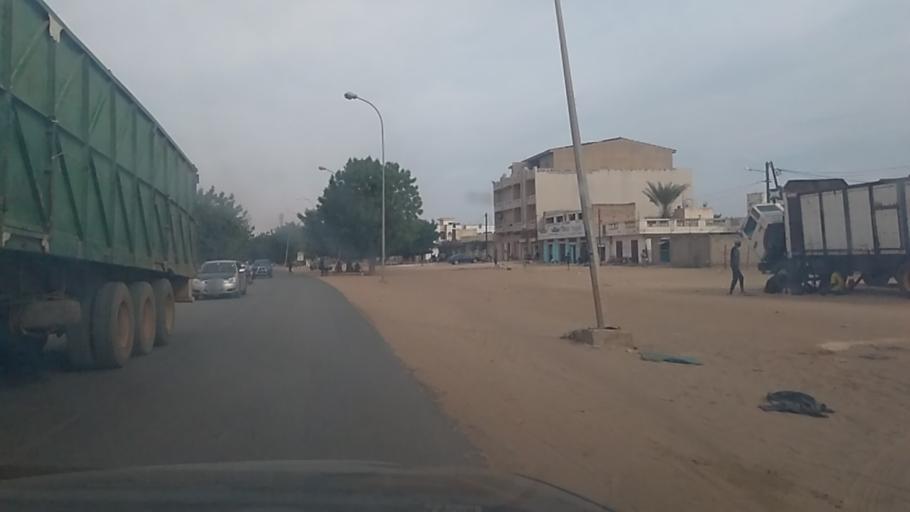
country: SN
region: Diourbel
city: Touba
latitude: 14.8387
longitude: -15.8774
